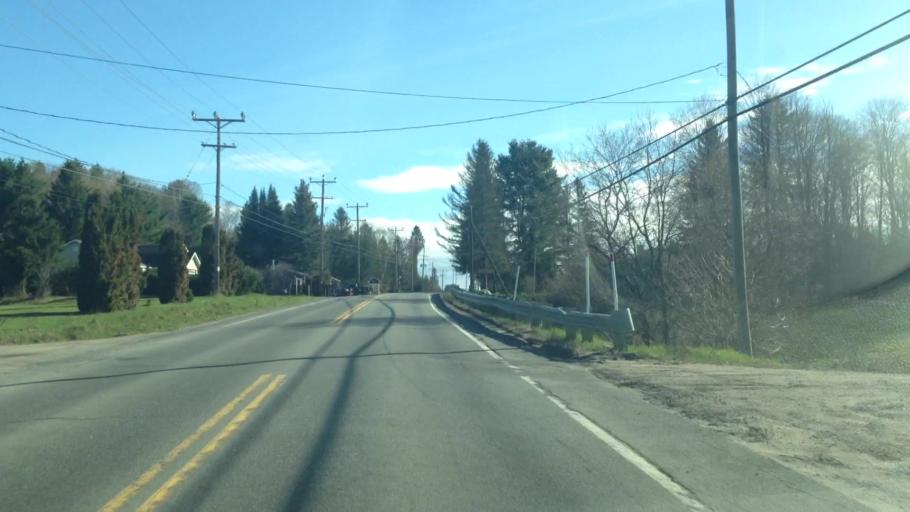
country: CA
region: Quebec
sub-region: Laurentides
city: Sainte-Adele
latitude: 45.9613
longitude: -74.1252
